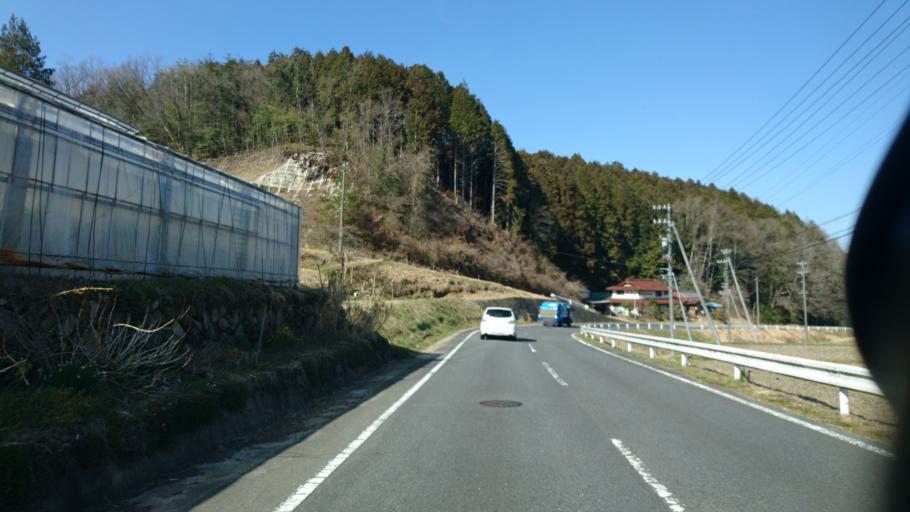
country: JP
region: Gifu
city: Nakatsugawa
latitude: 35.4607
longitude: 137.3750
